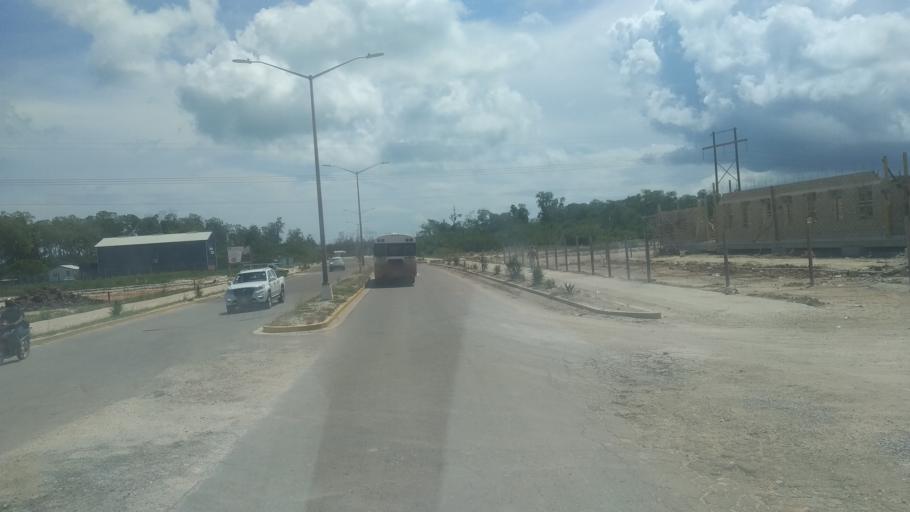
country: BZ
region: Belize
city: Belize City
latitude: 17.5043
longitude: -88.2220
